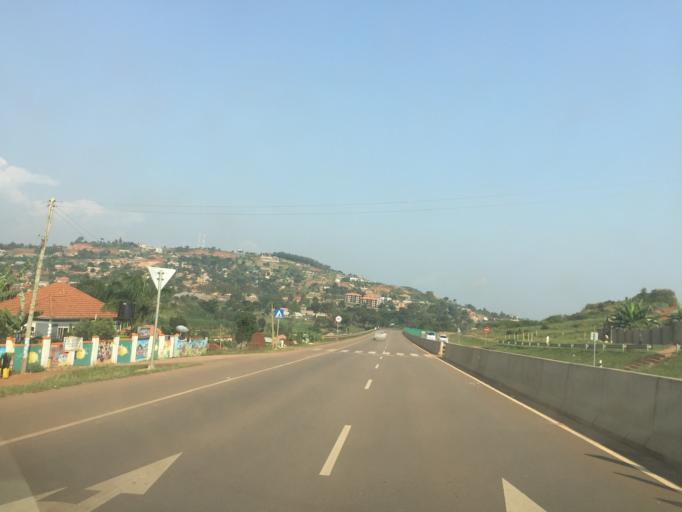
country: UG
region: Central Region
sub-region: Wakiso District
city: Kajansi
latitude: 0.2107
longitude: 32.5803
